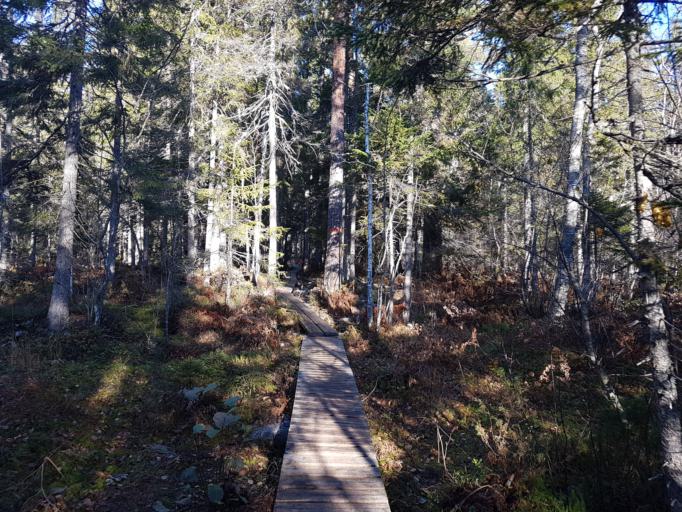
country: SE
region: Vaesternorrland
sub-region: OErnskoeldsviks Kommun
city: Kopmanholmen
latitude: 63.0930
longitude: 18.5011
